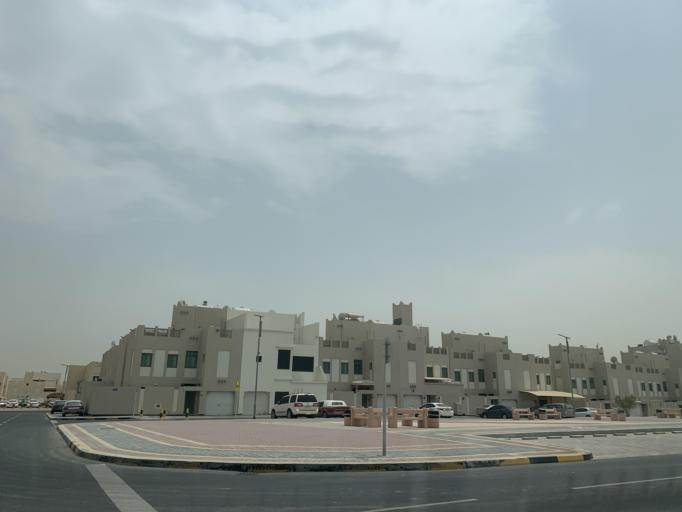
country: BH
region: Northern
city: Madinat `Isa
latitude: 26.1730
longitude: 50.5104
